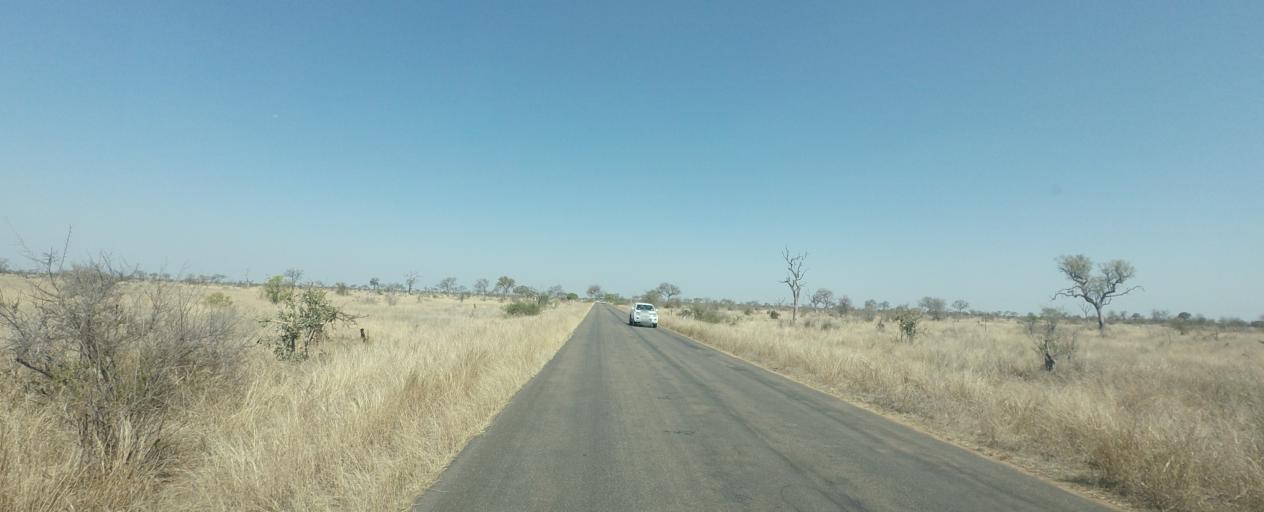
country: ZA
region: Limpopo
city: Thulamahashi
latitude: -24.3926
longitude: 31.7328
